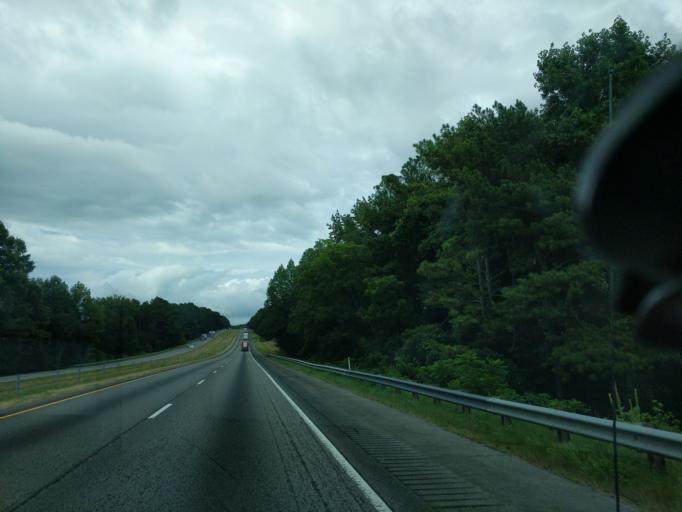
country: US
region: Georgia
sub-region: Jackson County
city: Braselton
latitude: 34.1297
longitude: -83.6991
